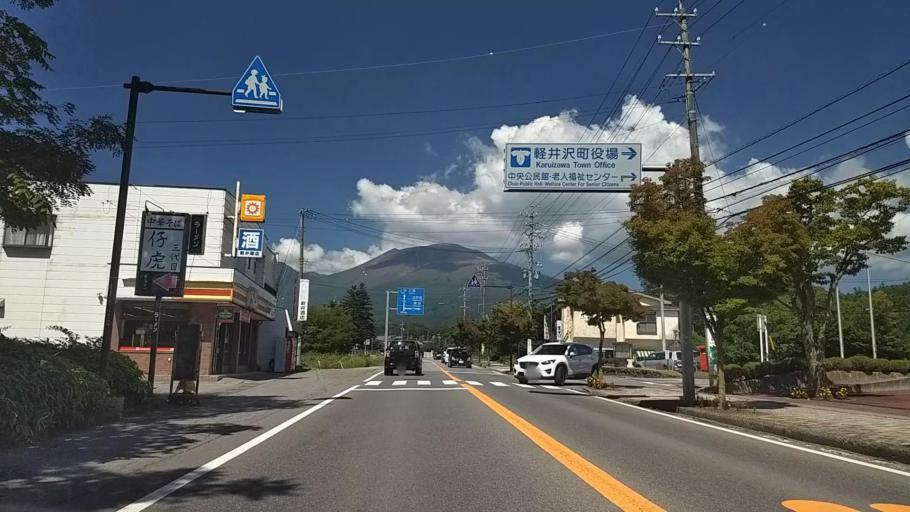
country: JP
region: Nagano
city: Komoro
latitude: 36.3479
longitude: 138.5968
